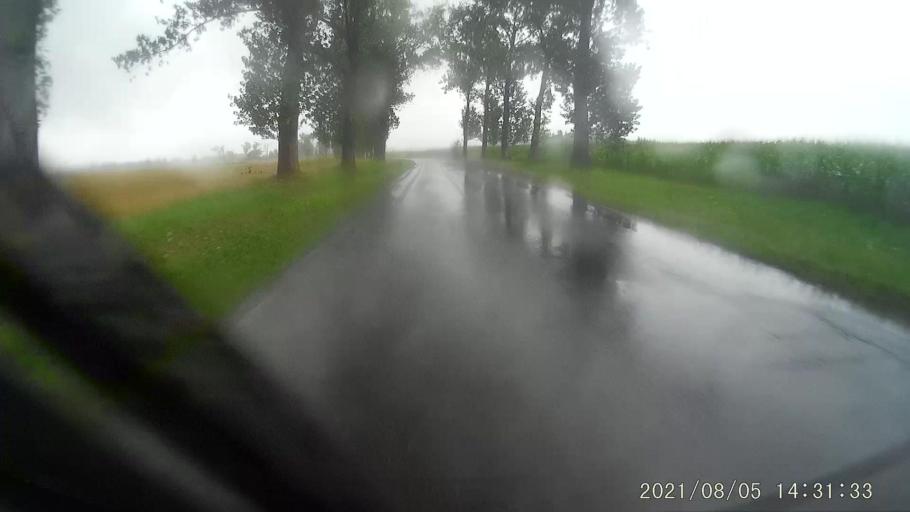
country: PL
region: Opole Voivodeship
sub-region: Powiat nyski
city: Korfantow
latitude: 50.4737
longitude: 17.5558
